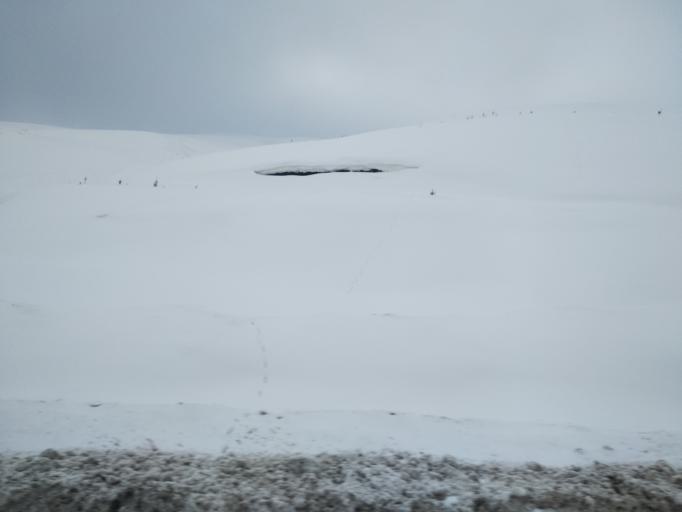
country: TR
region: Erzincan
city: Catalarmut
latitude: 39.8892
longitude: 39.3540
